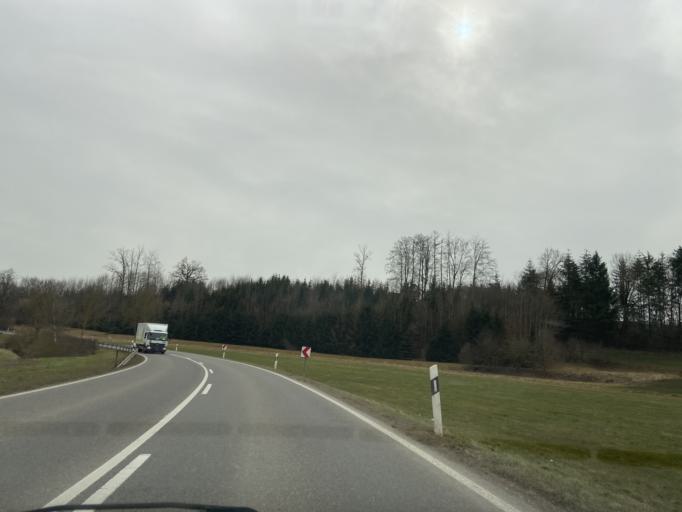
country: DE
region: Baden-Wuerttemberg
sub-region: Tuebingen Region
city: Ostrach
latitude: 47.9577
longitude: 9.3747
